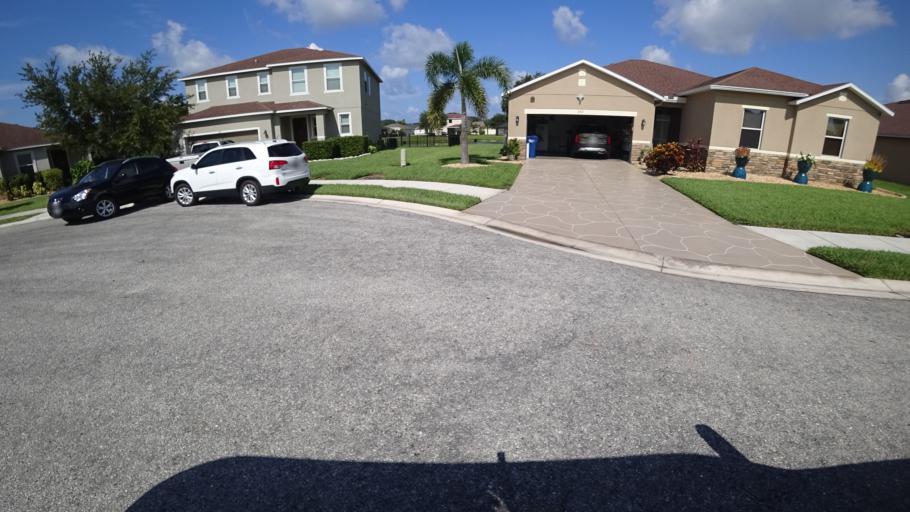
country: US
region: Florida
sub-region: Manatee County
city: Whitfield
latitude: 27.4274
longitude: -82.5604
